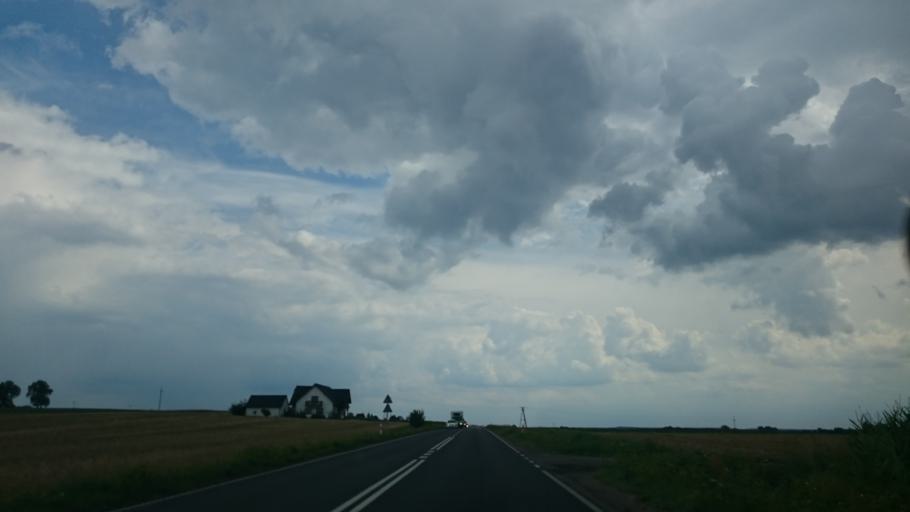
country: PL
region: Pomeranian Voivodeship
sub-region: Powiat chojnicki
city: Chojnice
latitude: 53.6672
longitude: 17.6638
